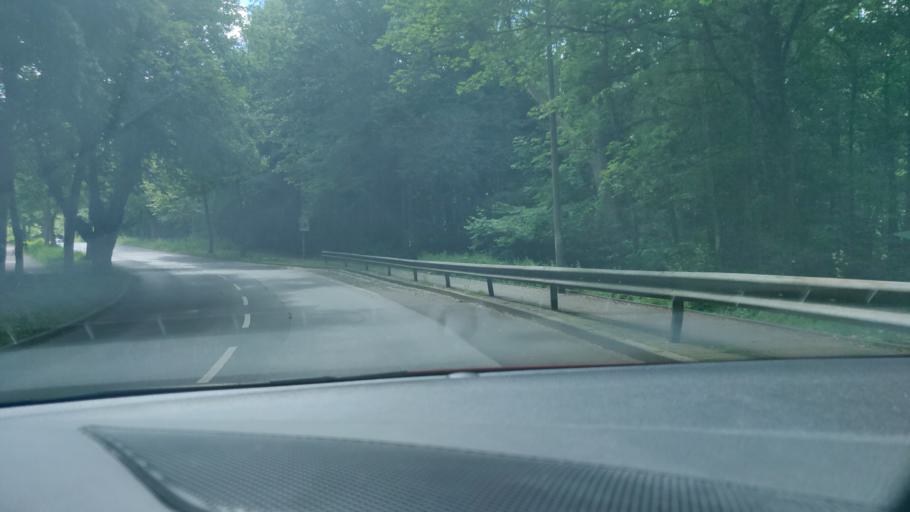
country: DE
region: North Rhine-Westphalia
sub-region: Regierungsbezirk Dusseldorf
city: Heiligenhaus
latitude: 51.3245
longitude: 6.9776
